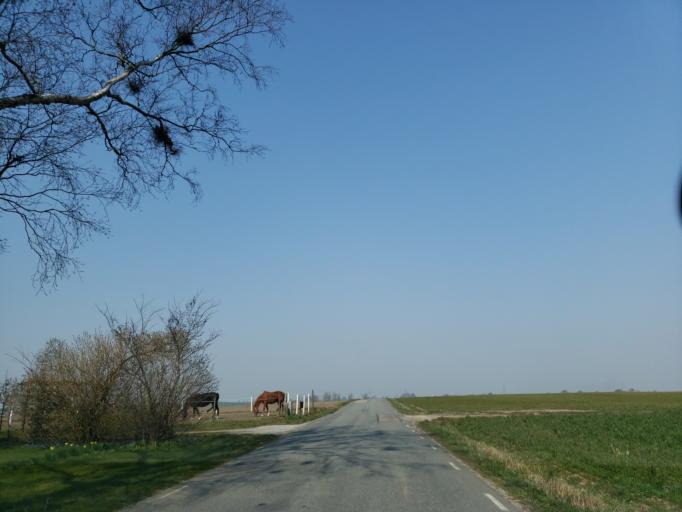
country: SE
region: Skane
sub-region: Simrishamns Kommun
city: Simrishamn
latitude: 55.4575
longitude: 14.2125
